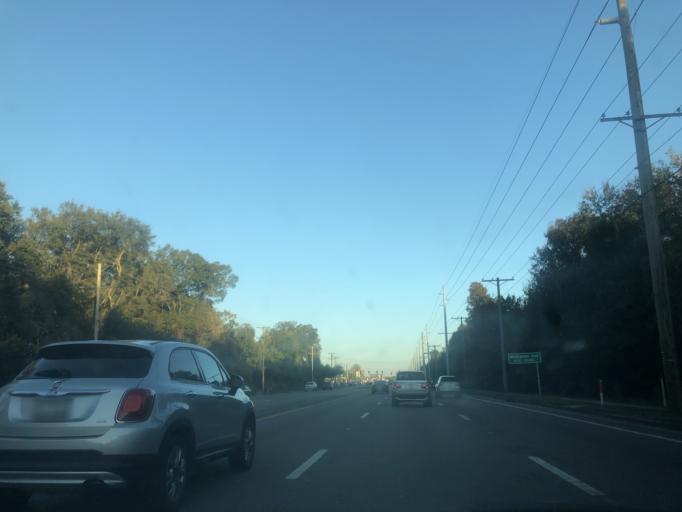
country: US
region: Florida
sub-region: Hillsborough County
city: Egypt Lake-Leto
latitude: 28.0254
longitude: -82.5204
